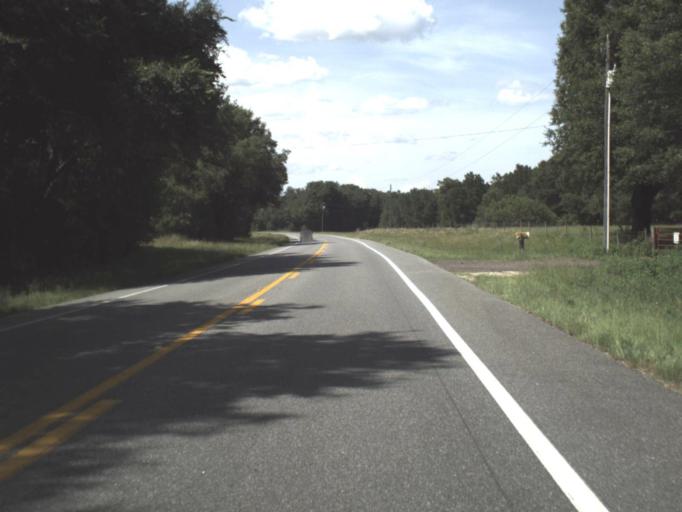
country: US
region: Florida
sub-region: Gilchrist County
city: Trenton
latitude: 29.7357
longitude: -82.7420
